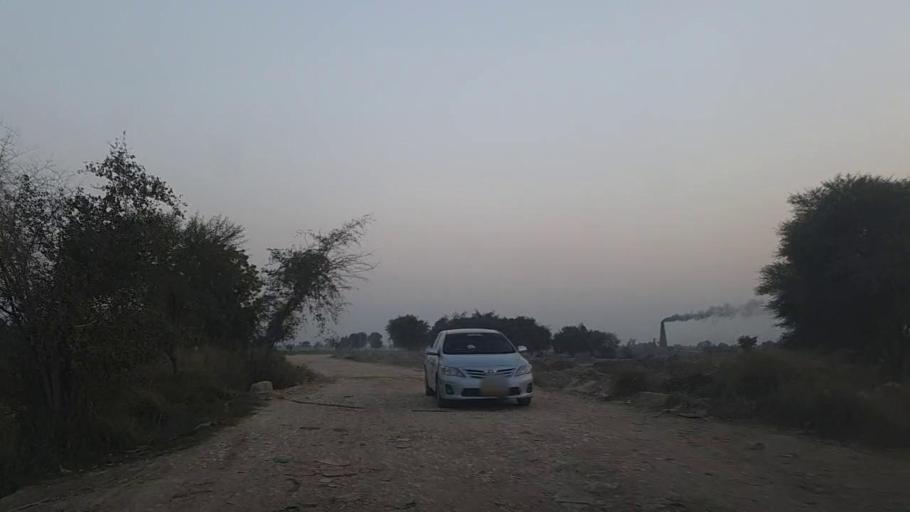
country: PK
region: Sindh
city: Naushahro Firoz
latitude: 26.8572
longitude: 68.0489
